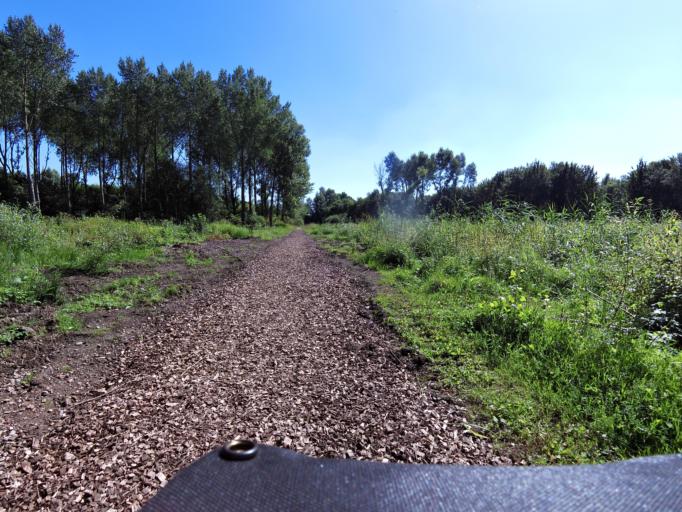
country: NL
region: South Holland
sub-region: Gemeente Dordrecht
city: Dordrecht
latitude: 51.7599
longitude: 4.6845
